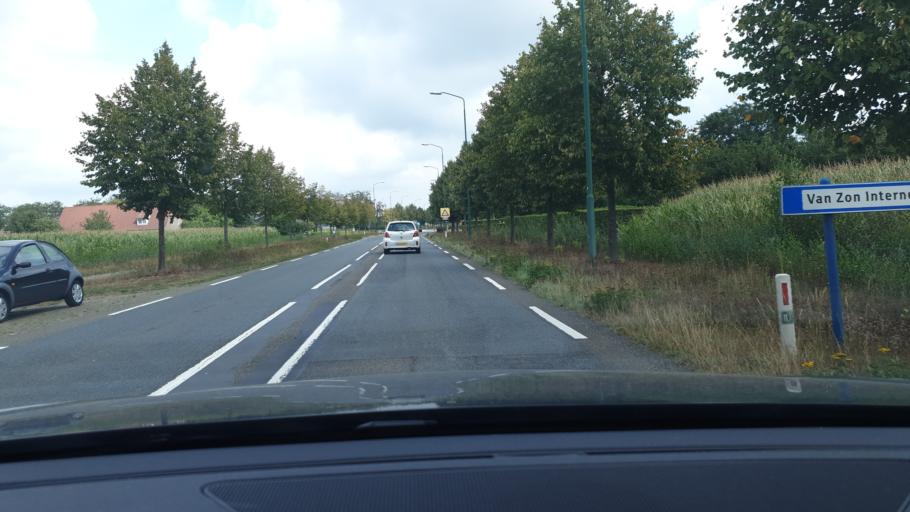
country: NL
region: North Brabant
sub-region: Gemeente Oirschot
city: Oostelbeers
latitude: 51.4832
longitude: 5.2789
